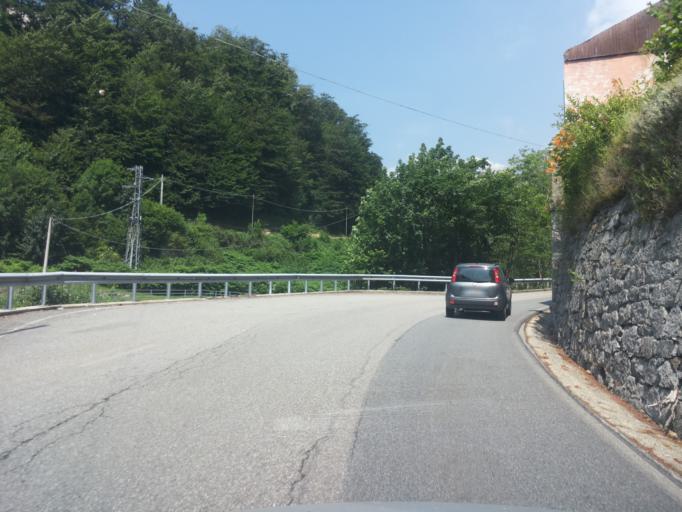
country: IT
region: Piedmont
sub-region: Provincia di Biella
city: San Paolo Cervo
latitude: 45.6513
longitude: 8.0130
